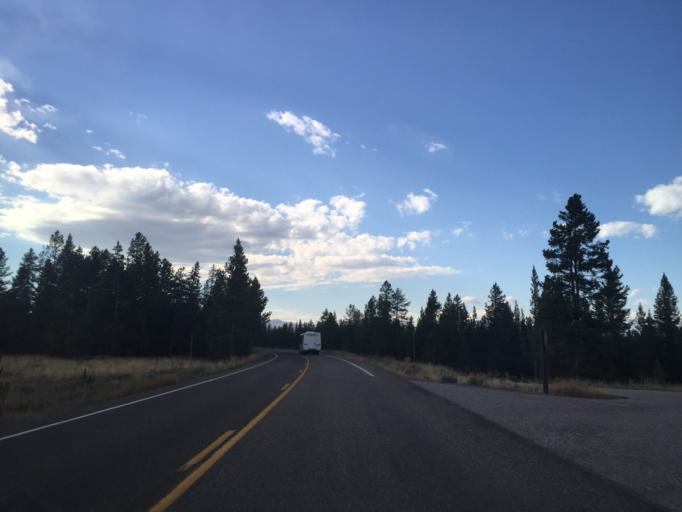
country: US
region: Montana
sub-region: Gallatin County
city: West Yellowstone
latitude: 44.6527
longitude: -111.0621
